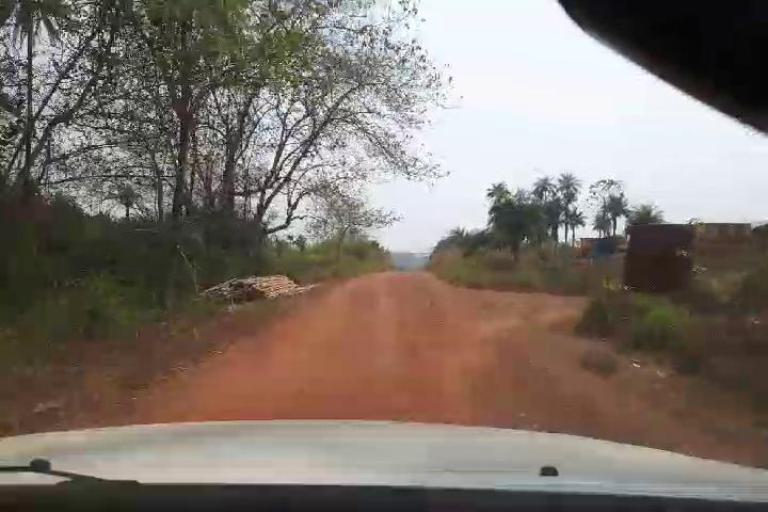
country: SL
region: Northern Province
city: Bumbuna
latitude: 8.9455
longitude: -11.8131
